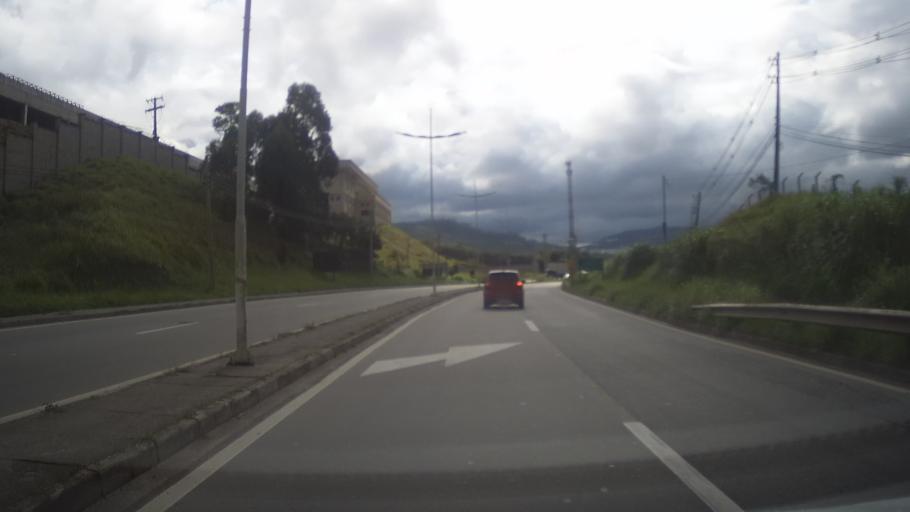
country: BR
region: Sao Paulo
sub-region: Cajamar
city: Cajamar
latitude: -23.3442
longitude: -46.8354
